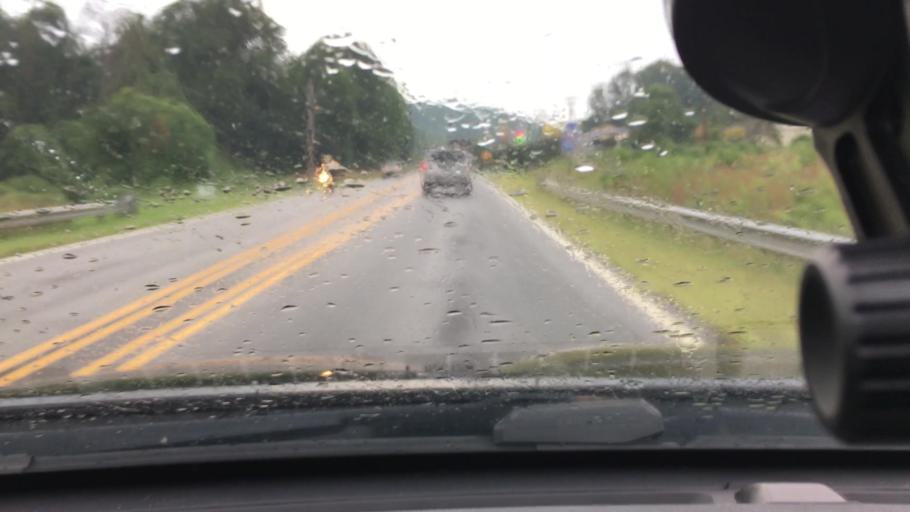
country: US
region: North Carolina
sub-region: McDowell County
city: West Marion
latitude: 35.6382
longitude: -81.9860
